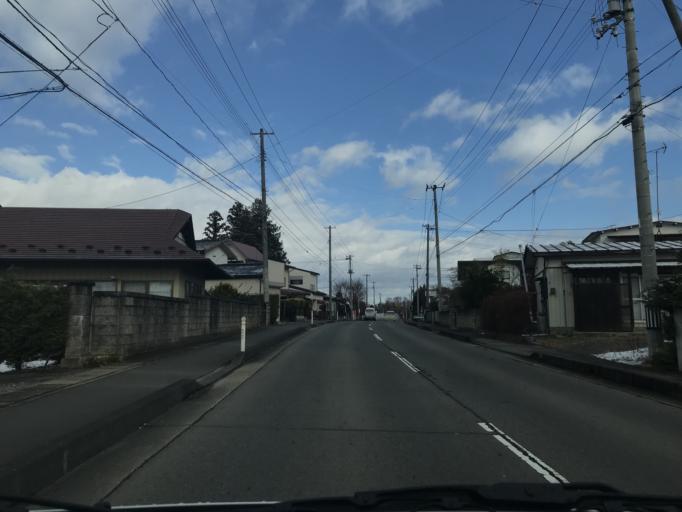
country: JP
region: Iwate
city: Mizusawa
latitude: 39.1168
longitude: 141.1378
